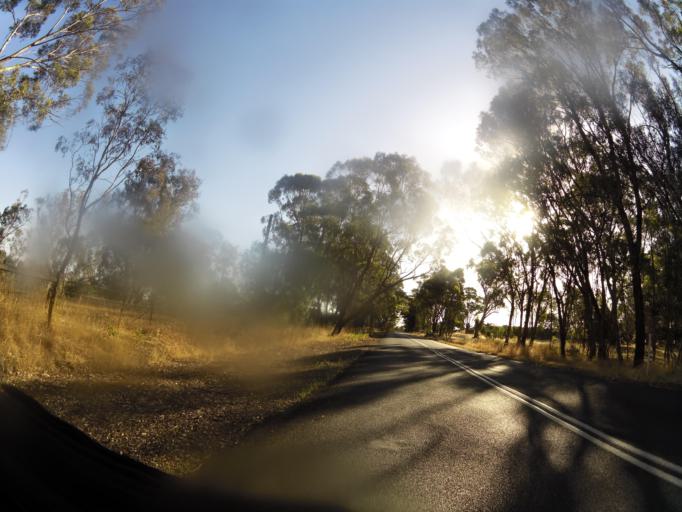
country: AU
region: Victoria
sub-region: Murrindindi
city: Kinglake West
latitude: -37.0205
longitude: 145.1069
